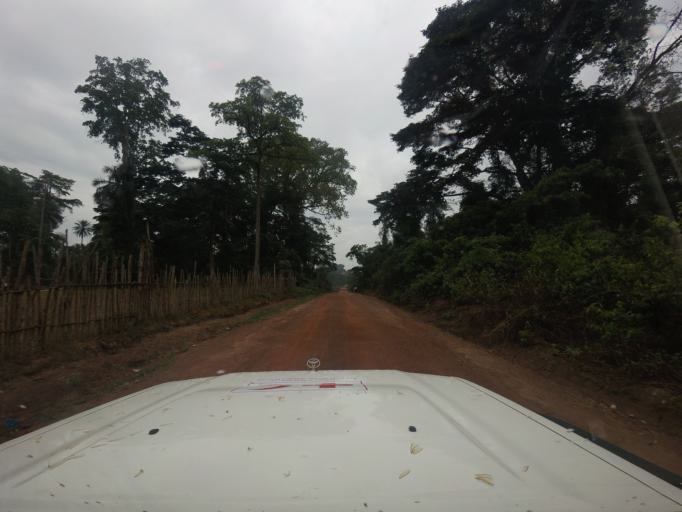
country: LR
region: Lofa
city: Voinjama
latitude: 8.3765
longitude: -9.8524
